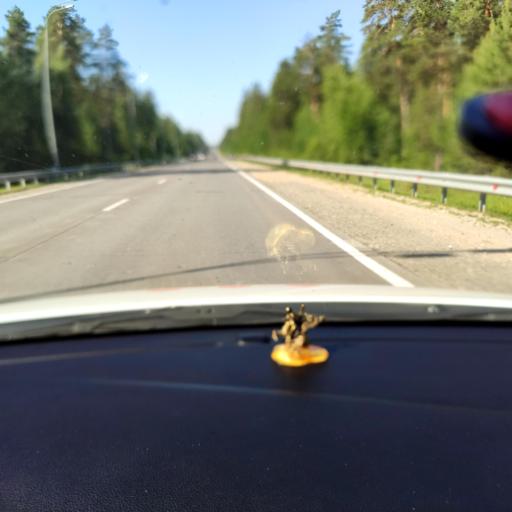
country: RU
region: Tatarstan
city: Stolbishchi
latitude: 55.6561
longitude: 49.1485
